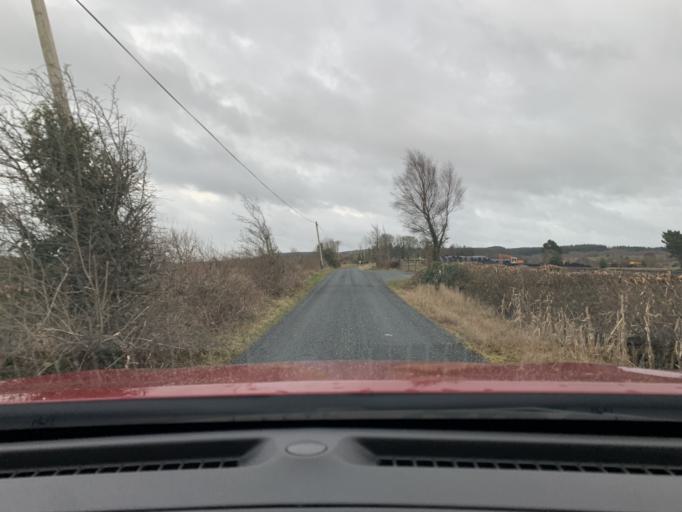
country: IE
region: Connaught
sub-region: Roscommon
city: Ballaghaderreen
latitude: 53.9692
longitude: -8.5212
